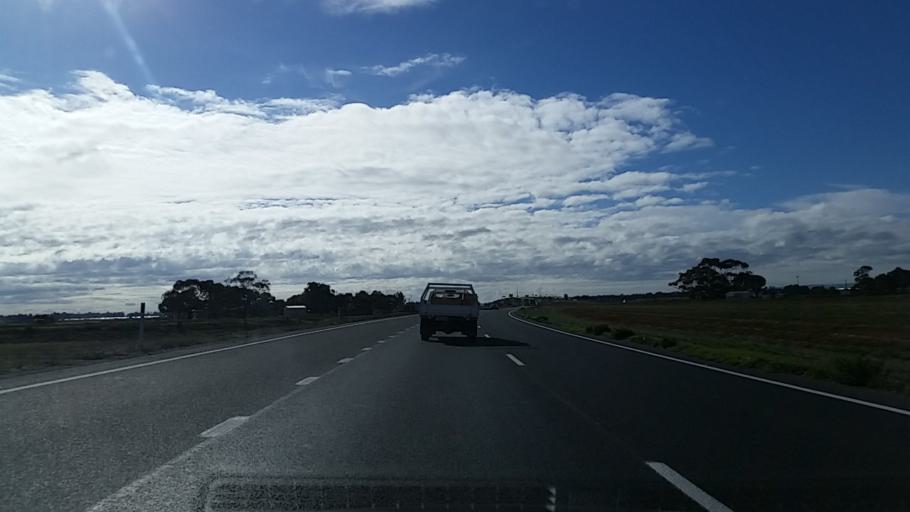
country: AU
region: South Australia
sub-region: Playford
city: Virginia
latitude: -34.6969
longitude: 138.5781
